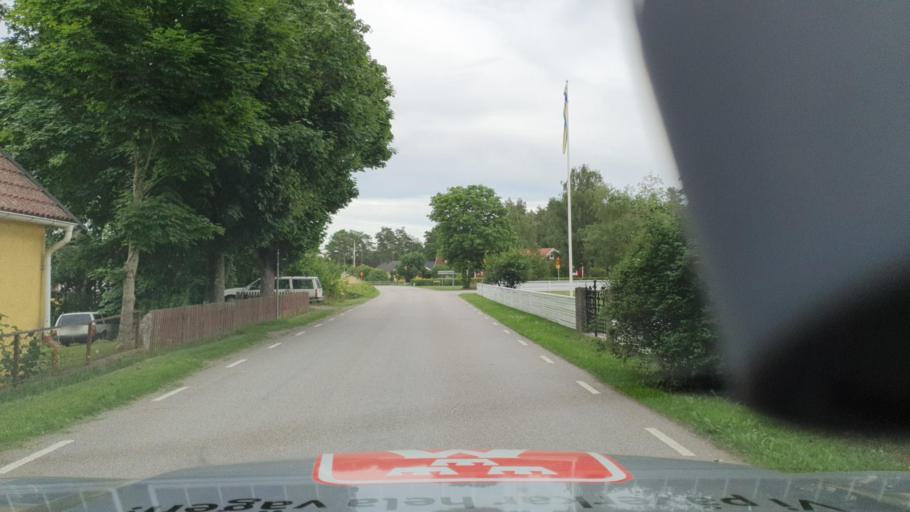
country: SE
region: Kalmar
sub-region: Kalmar Kommun
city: Trekanten
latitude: 56.6182
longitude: 16.0494
